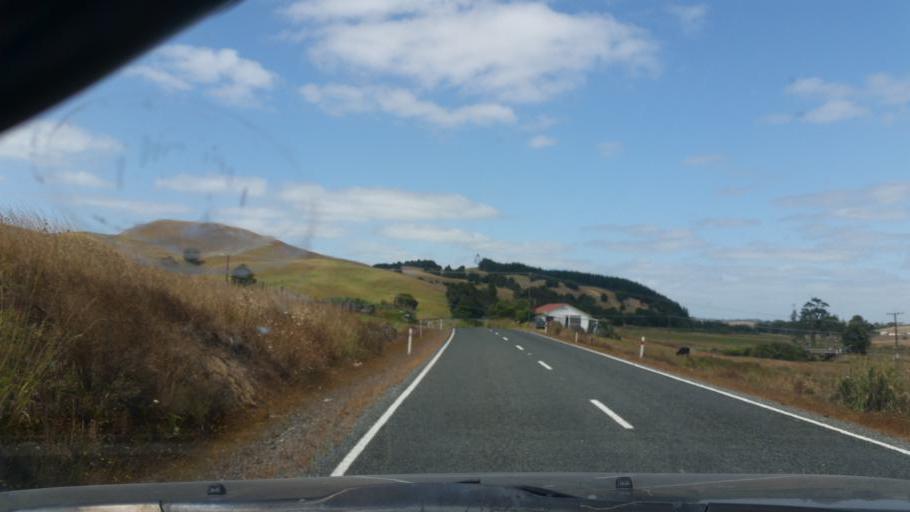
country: NZ
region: Northland
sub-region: Whangarei
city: Ruakaka
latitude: -35.9623
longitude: 174.2907
